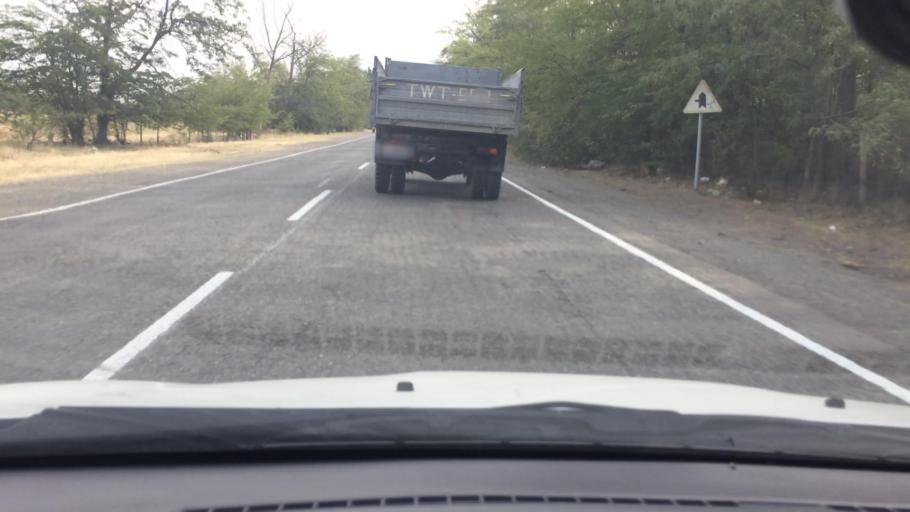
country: GE
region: Kvemo Kartli
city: Rust'avi
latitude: 41.4723
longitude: 44.9781
